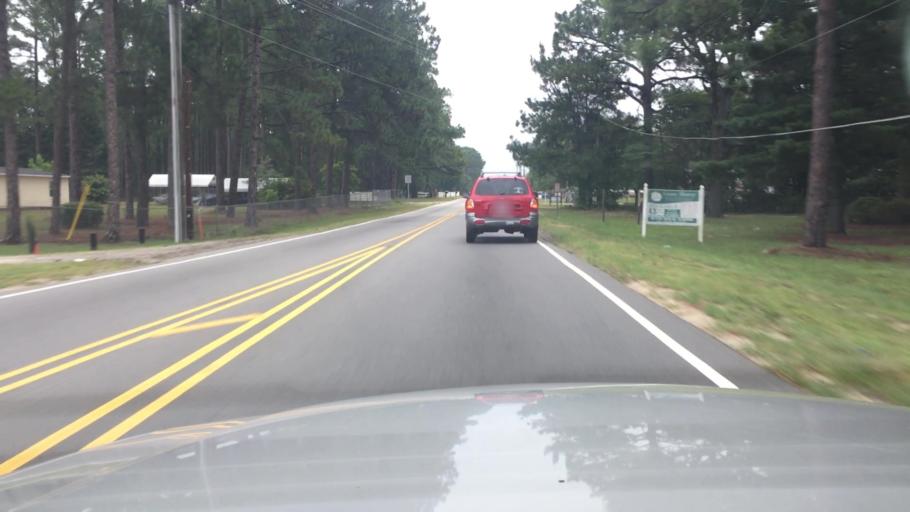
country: US
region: North Carolina
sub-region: Cumberland County
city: Hope Mills
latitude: 34.9780
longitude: -78.9840
